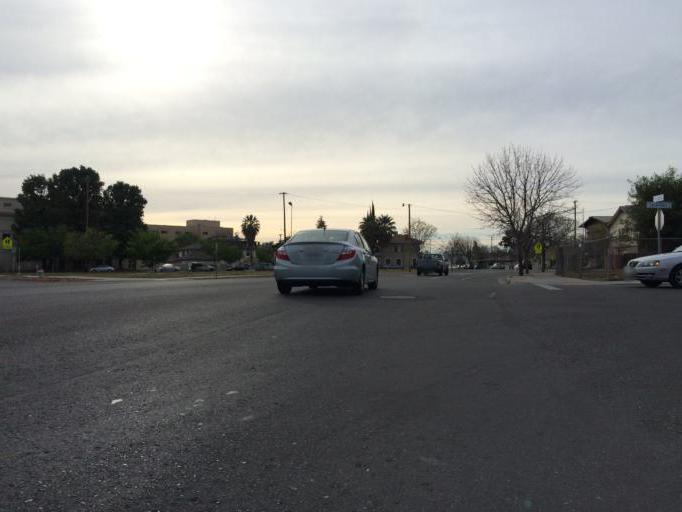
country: US
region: California
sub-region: Fresno County
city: Fresno
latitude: 36.7434
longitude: -119.7916
